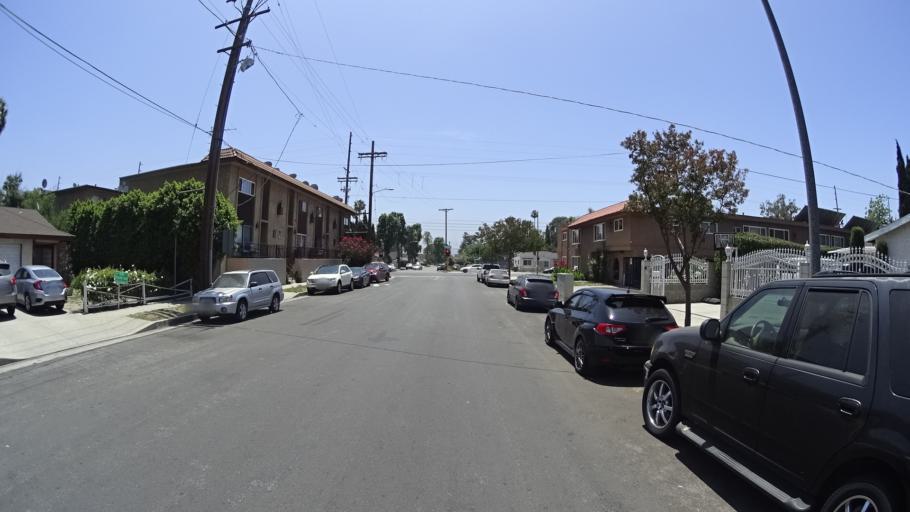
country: US
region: California
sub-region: Los Angeles County
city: Van Nuys
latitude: 34.1946
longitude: -118.4357
